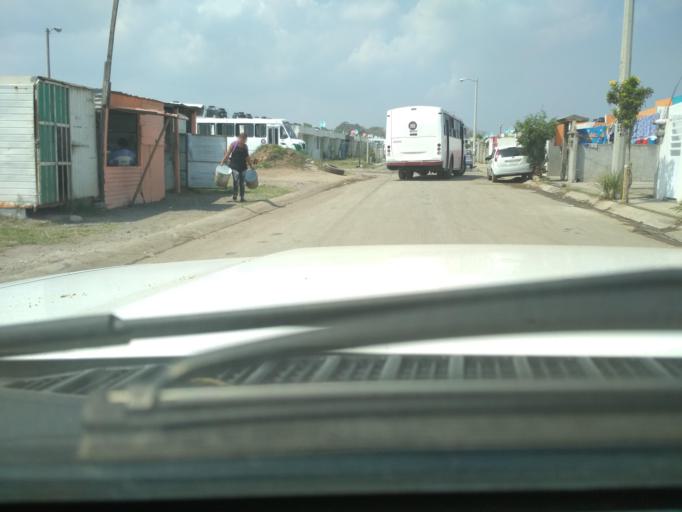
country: MX
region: Veracruz
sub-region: Veracruz
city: Lomas de Rio Medio Cuatro
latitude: 19.1864
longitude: -96.2089
